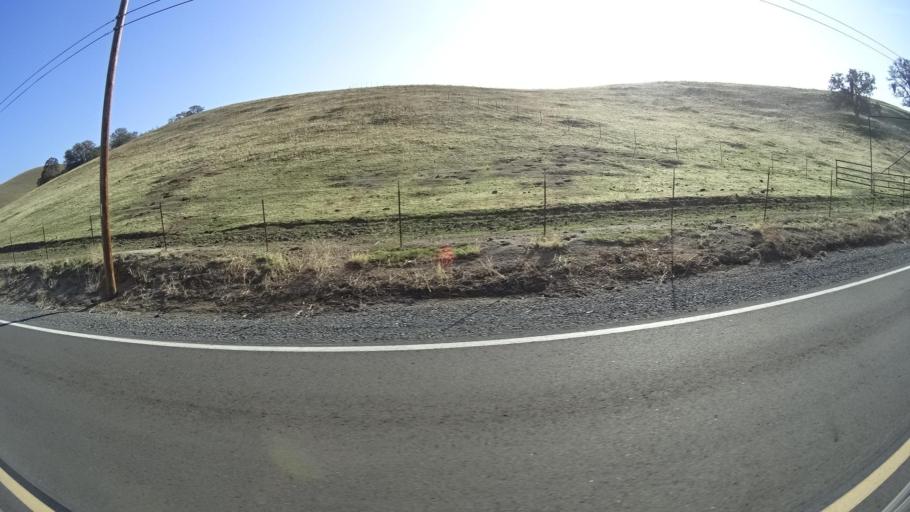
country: US
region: California
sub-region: Tulare County
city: Richgrove
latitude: 35.7177
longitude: -118.8607
